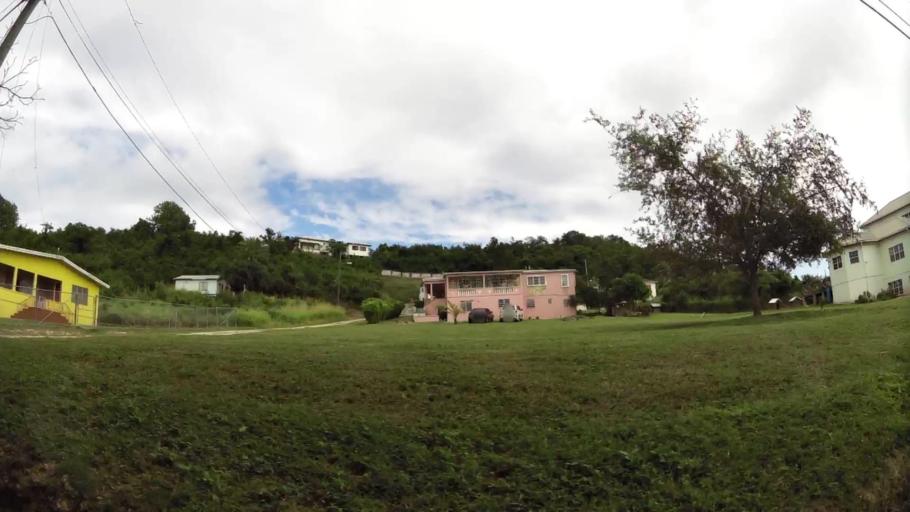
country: AG
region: Saint John
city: Potters Village
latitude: 17.0883
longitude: -61.8111
